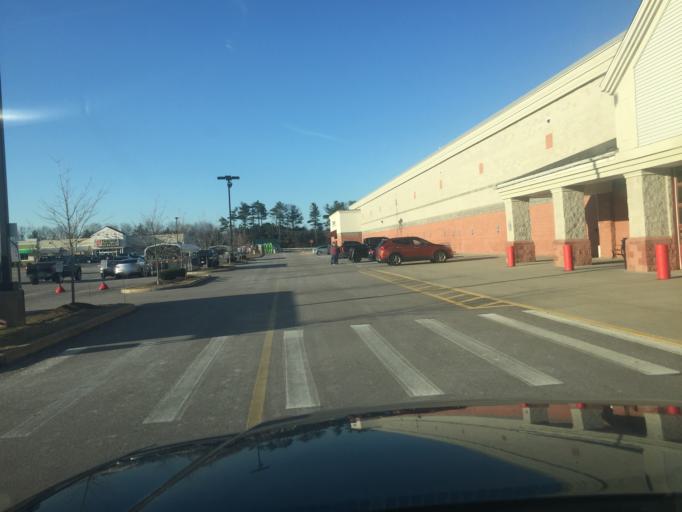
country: US
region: Massachusetts
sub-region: Bristol County
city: Raynham
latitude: 41.9593
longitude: -71.1169
